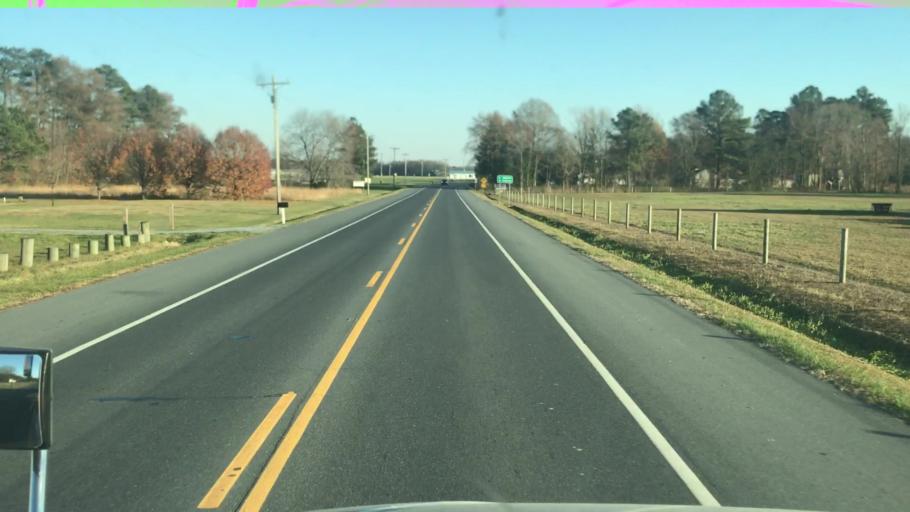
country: US
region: Delaware
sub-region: Sussex County
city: Bridgeville
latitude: 38.7827
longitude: -75.6719
